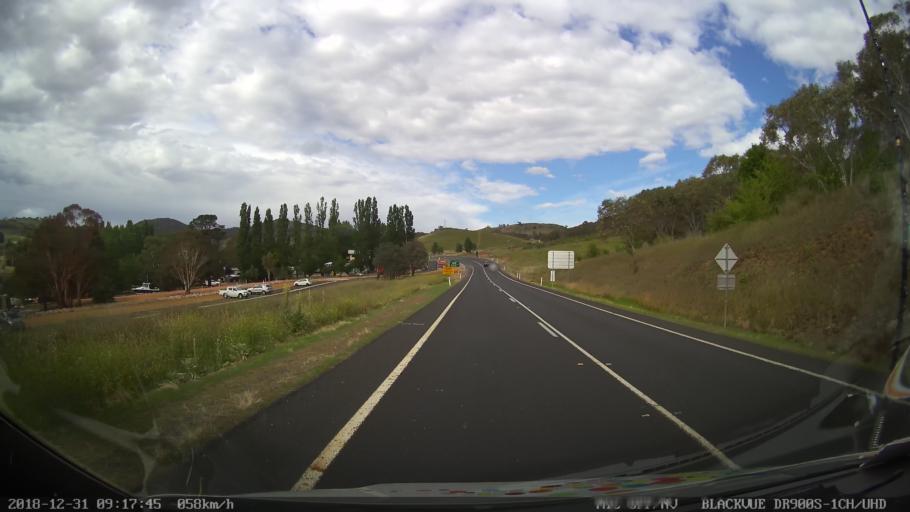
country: AU
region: New South Wales
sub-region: Snowy River
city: Jindabyne
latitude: -36.4084
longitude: 148.5988
